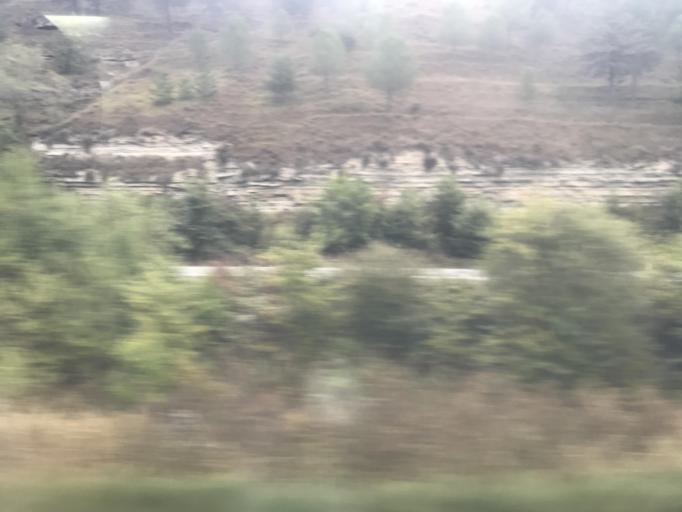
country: ES
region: Castille and Leon
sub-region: Provincia de Burgos
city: Briviesca
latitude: 42.5260
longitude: -3.3304
